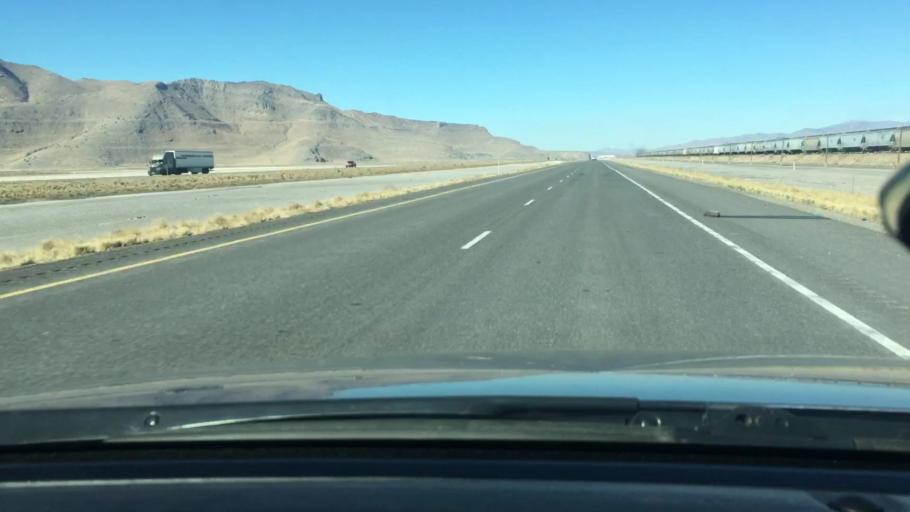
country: US
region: Utah
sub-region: Tooele County
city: Grantsville
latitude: 40.7262
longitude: -112.5738
